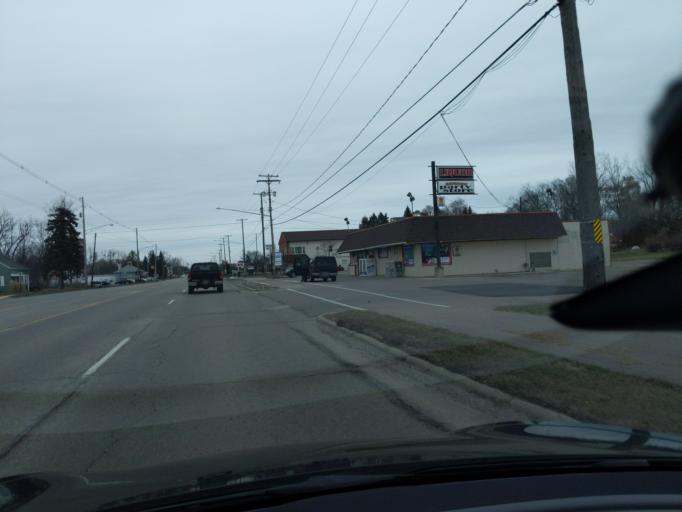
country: US
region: Michigan
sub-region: Ingham County
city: Lansing
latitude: 42.7820
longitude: -84.5426
